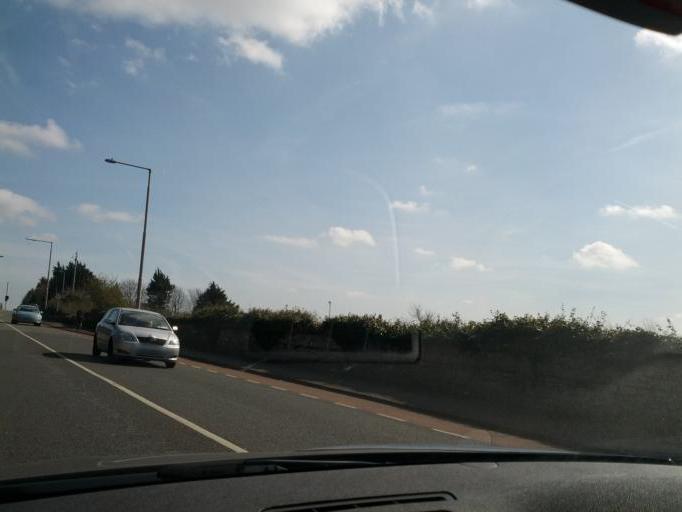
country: IE
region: Leinster
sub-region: Kildare
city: Leixlip
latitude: 53.3703
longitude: -6.5094
